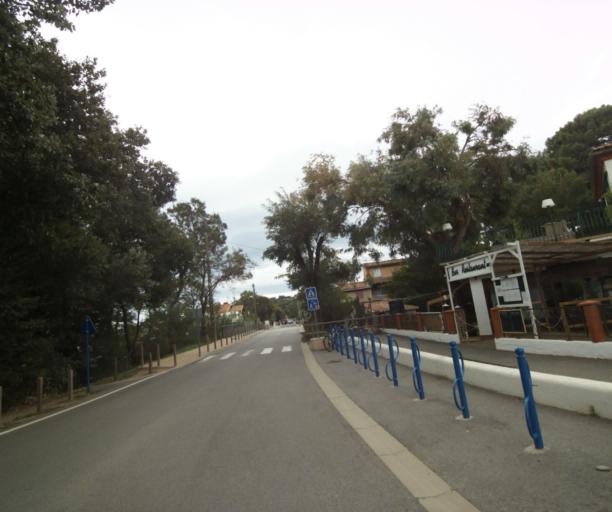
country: FR
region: Languedoc-Roussillon
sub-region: Departement des Pyrenees-Orientales
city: Argelers
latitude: 42.5389
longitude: 3.0524
